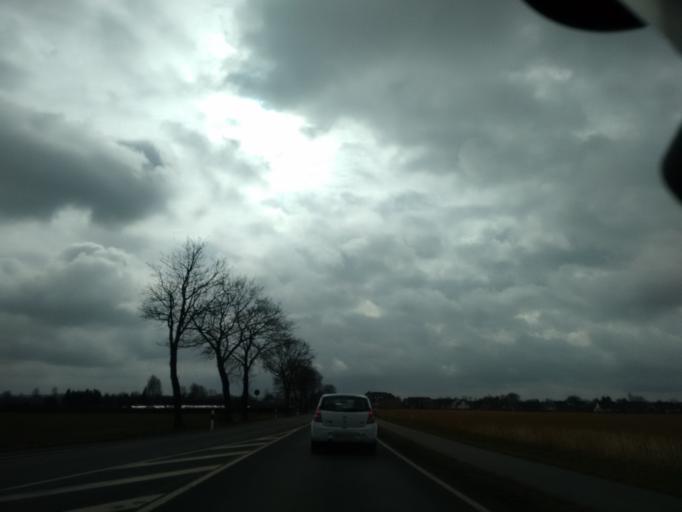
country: DE
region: North Rhine-Westphalia
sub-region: Regierungsbezirk Detmold
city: Paderborn
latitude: 51.7493
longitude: 8.7764
